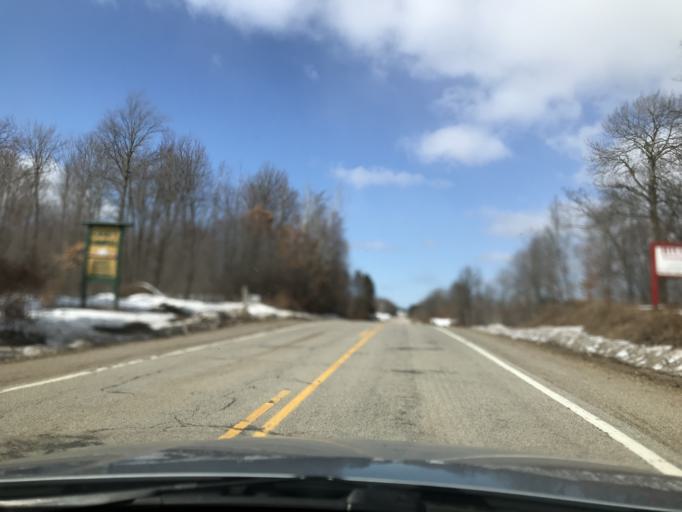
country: US
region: Wisconsin
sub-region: Oconto County
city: Oconto Falls
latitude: 45.2881
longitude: -88.1031
